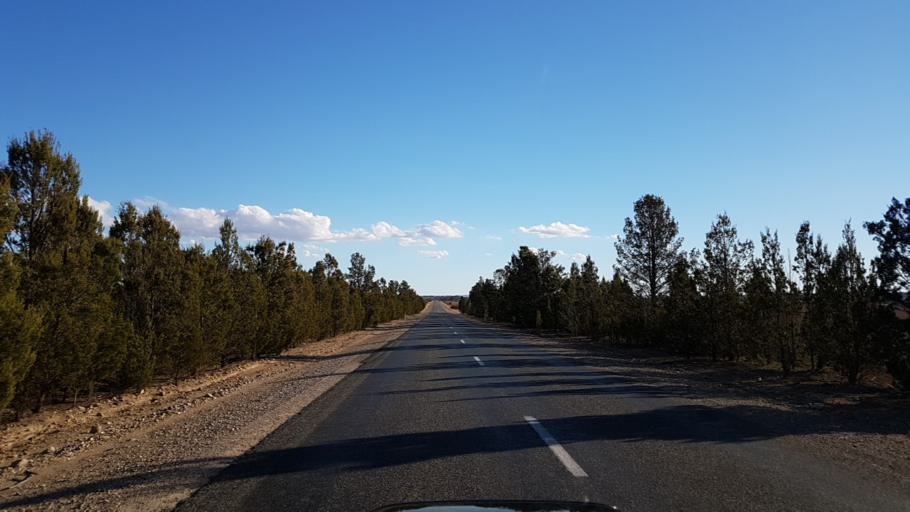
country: AU
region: South Australia
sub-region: Peterborough
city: Peterborough
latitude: -32.9621
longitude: 138.8869
